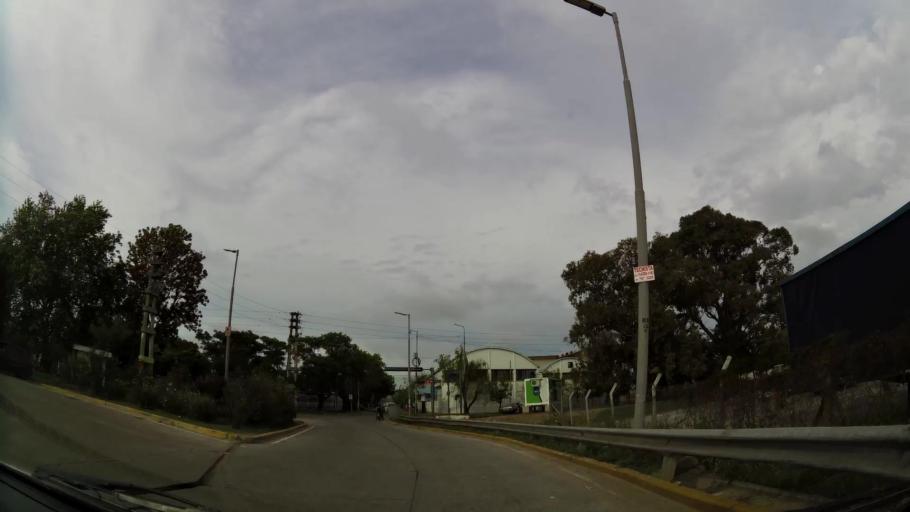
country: AR
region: Buenos Aires
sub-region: Partido de Quilmes
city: Quilmes
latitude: -34.7031
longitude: -58.2763
